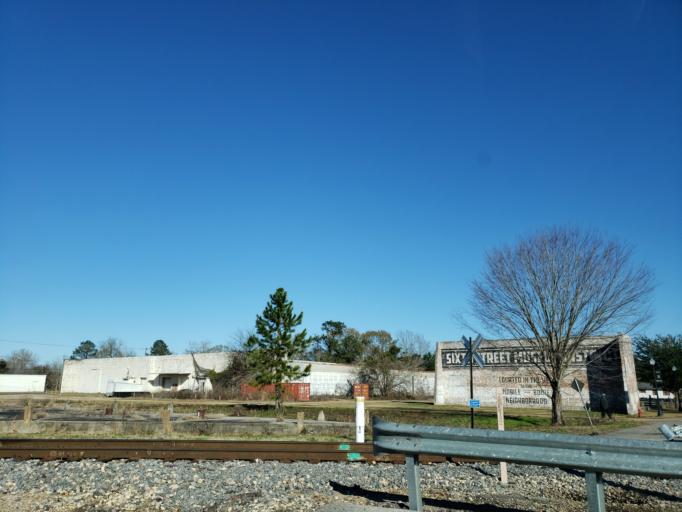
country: US
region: Mississippi
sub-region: Forrest County
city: Hattiesburg
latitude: 31.3346
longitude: -89.2944
